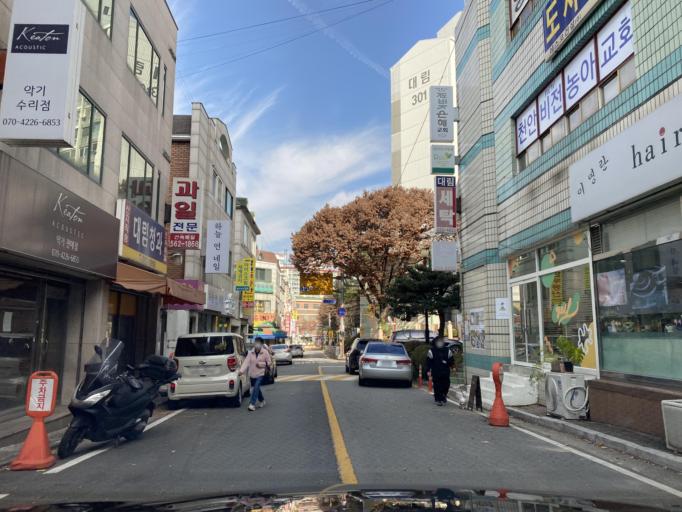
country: KR
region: Chungcheongnam-do
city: Cheonan
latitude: 36.8205
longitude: 127.1601
